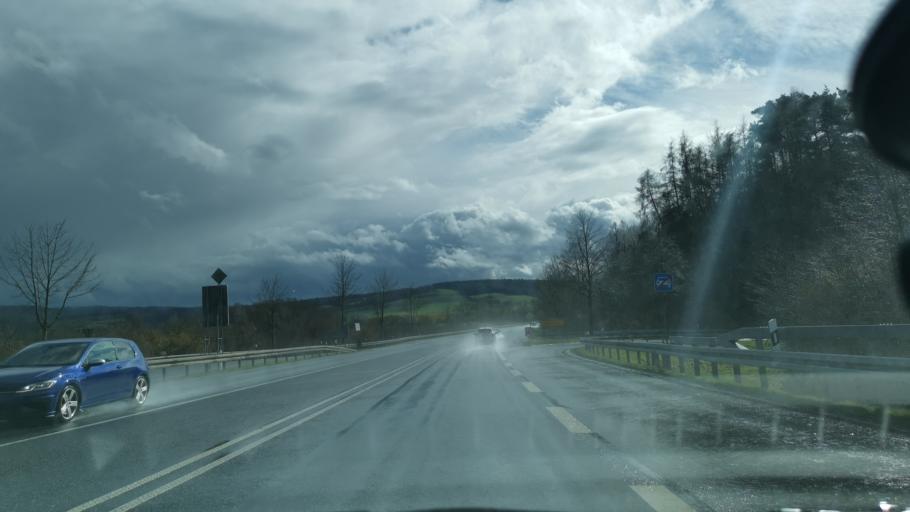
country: DE
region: Hesse
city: Breitenbach
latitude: 50.9339
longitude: 9.7719
